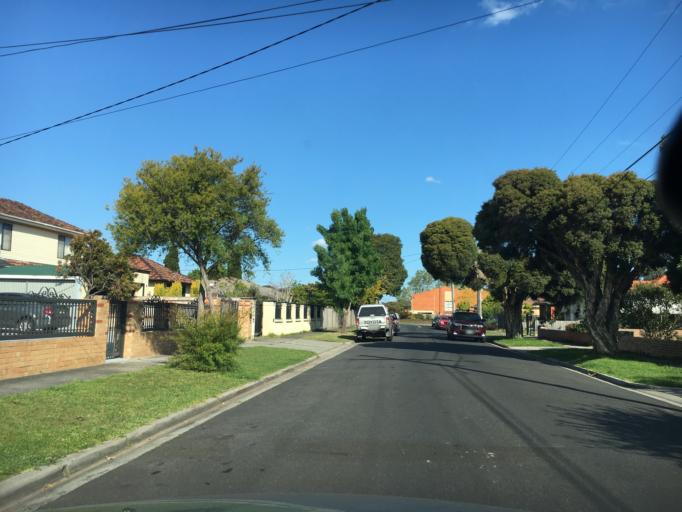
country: AU
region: Victoria
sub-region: Greater Dandenong
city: Springvale
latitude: -37.9386
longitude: 145.1533
